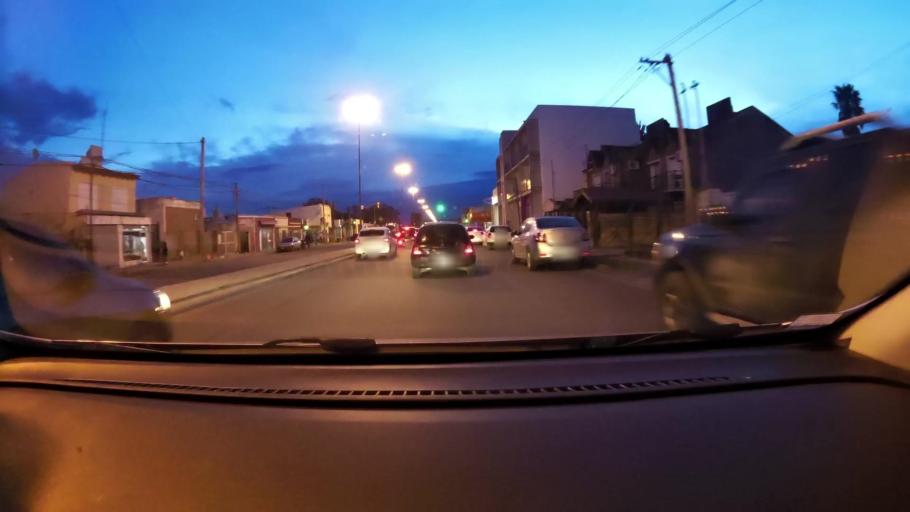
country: AR
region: Buenos Aires
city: San Nicolas de los Arroyos
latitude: -33.3529
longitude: -60.2413
